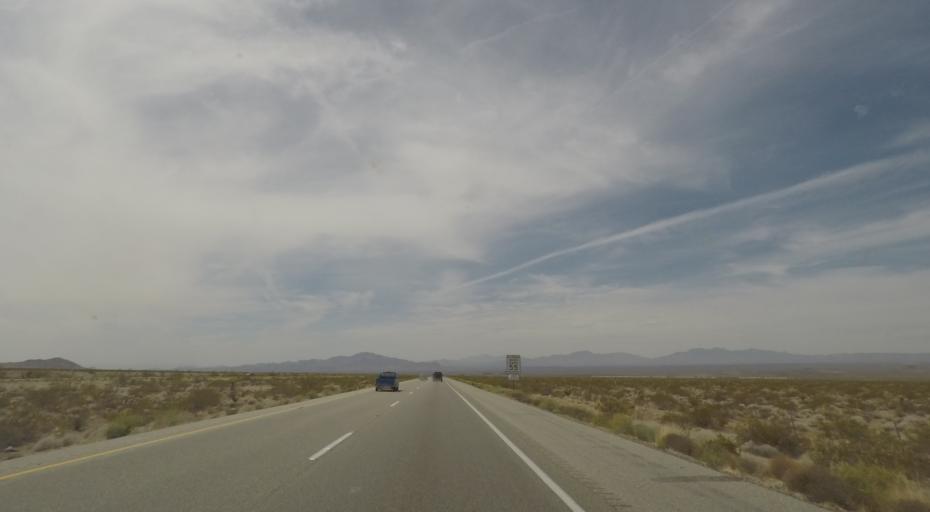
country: US
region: California
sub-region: San Bernardino County
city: Needles
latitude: 34.8227
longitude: -115.1087
